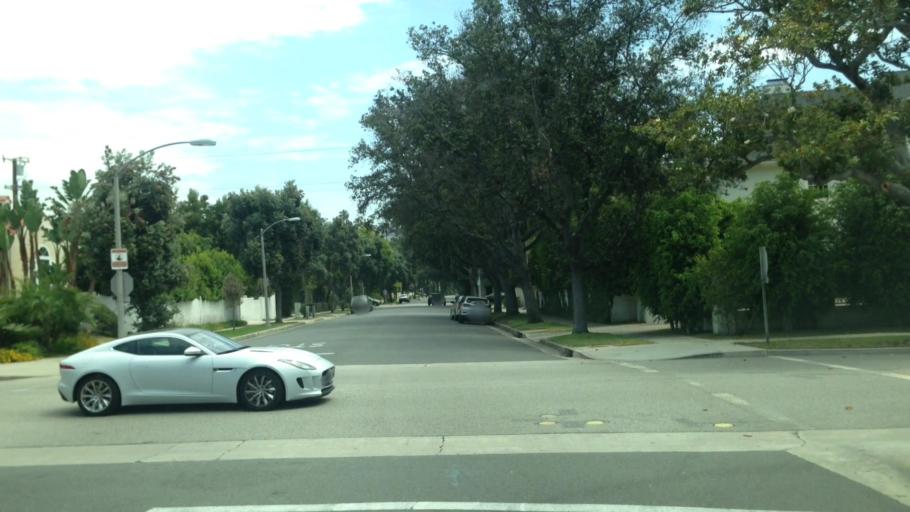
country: US
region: California
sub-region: Los Angeles County
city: Beverly Hills
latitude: 34.0742
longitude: -118.4119
